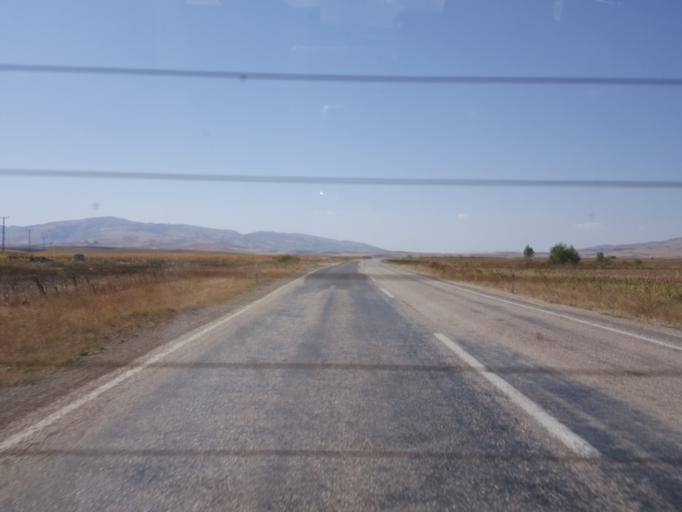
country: TR
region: Amasya
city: Dogantepe
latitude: 40.5783
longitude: 35.6279
